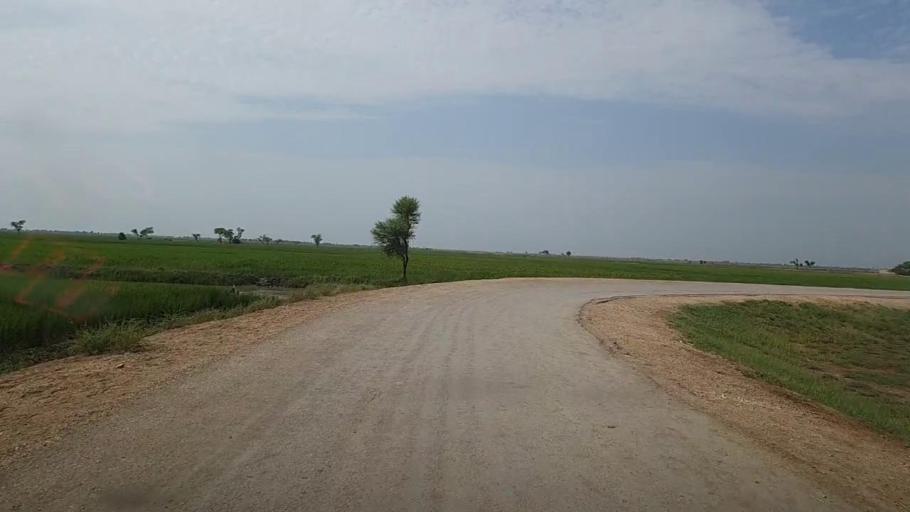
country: PK
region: Sindh
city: Thul
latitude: 28.2672
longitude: 68.8177
